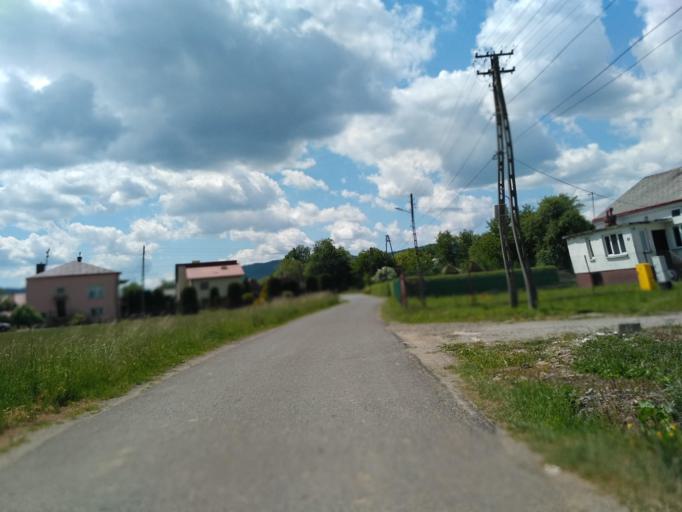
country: PL
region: Subcarpathian Voivodeship
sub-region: Powiat krosnienski
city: Dukla
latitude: 49.5639
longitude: 21.6959
